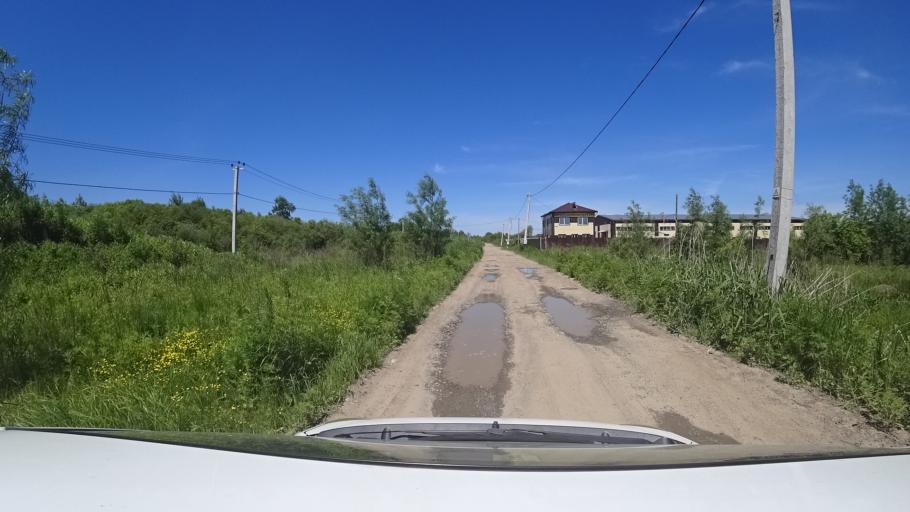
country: RU
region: Khabarovsk Krai
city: Topolevo
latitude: 48.4831
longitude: 135.1751
